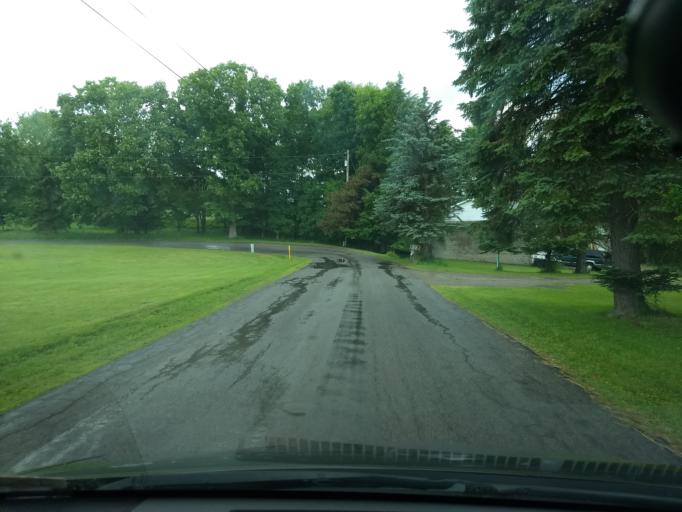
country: US
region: Pennsylvania
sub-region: Armstrong County
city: Orchard Hills
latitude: 40.5531
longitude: -79.5017
